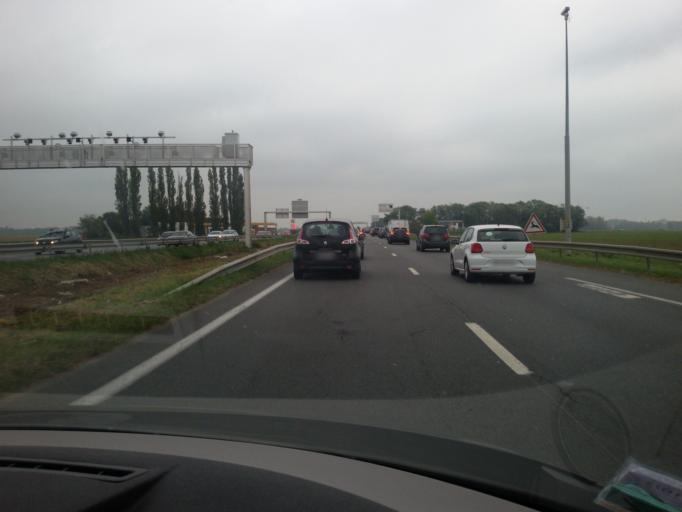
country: FR
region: Ile-de-France
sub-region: Departement de l'Essonne
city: Saclay
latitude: 48.7251
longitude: 2.1664
